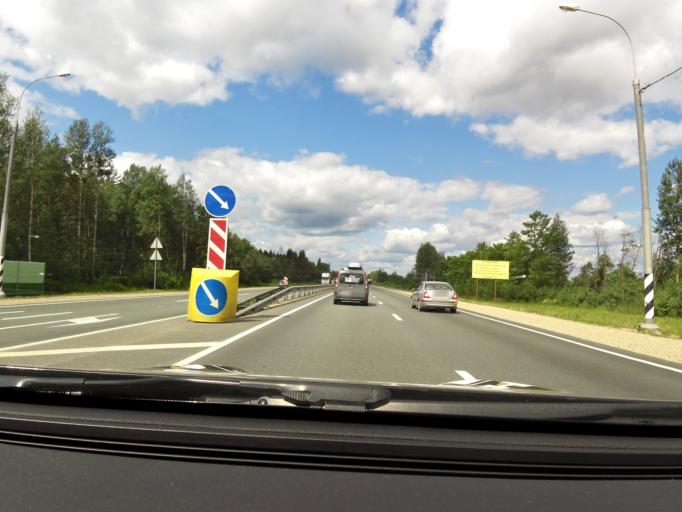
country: RU
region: Tverskaya
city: Torzhok
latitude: 57.0197
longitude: 35.0533
